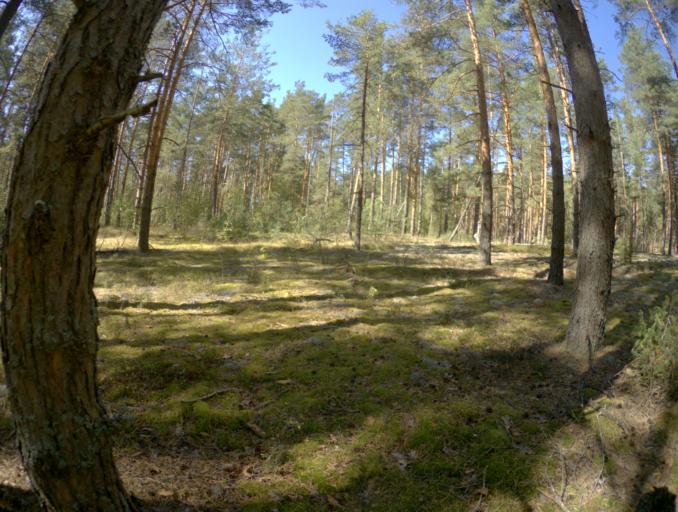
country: RU
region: Vladimir
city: Petushki
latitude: 55.8669
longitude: 39.3308
